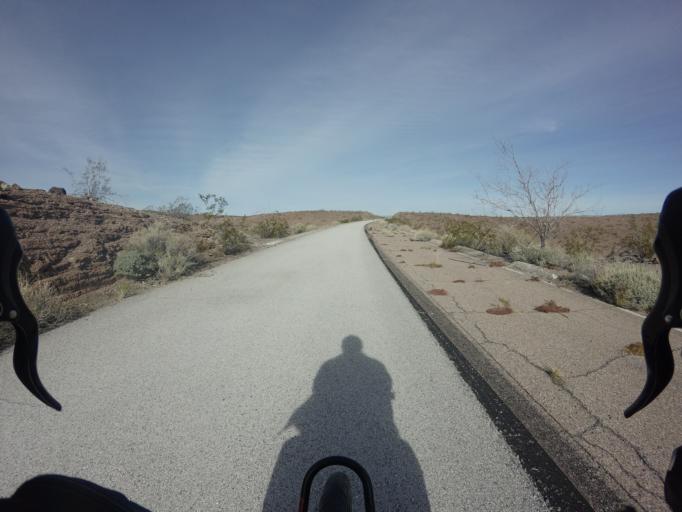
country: US
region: Nevada
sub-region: Clark County
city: Boulder City
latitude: 36.0911
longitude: -114.8403
